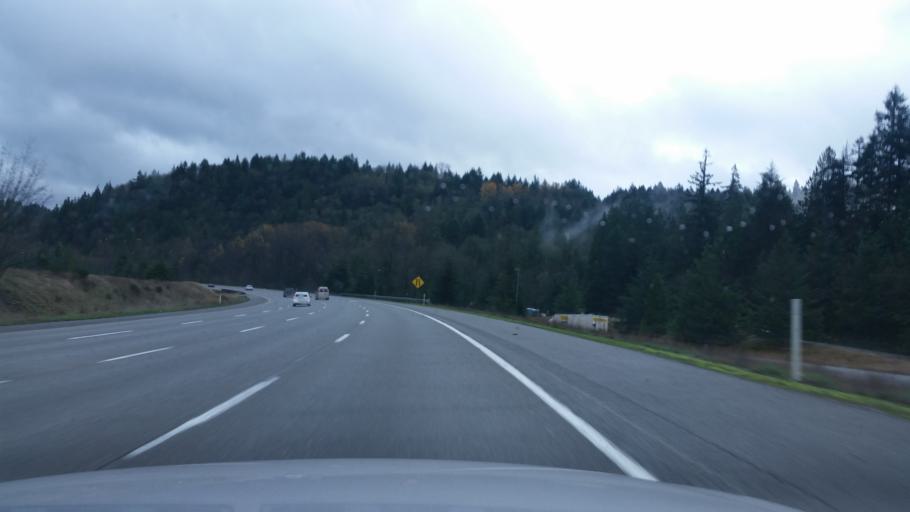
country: US
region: Washington
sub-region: King County
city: Issaquah
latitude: 47.5307
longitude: -121.9827
